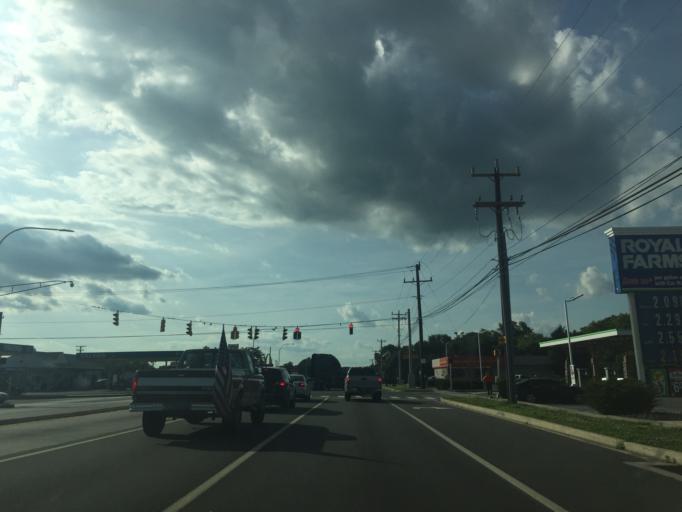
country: US
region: Delaware
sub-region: Kent County
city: Smyrna
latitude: 39.3057
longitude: -75.6064
